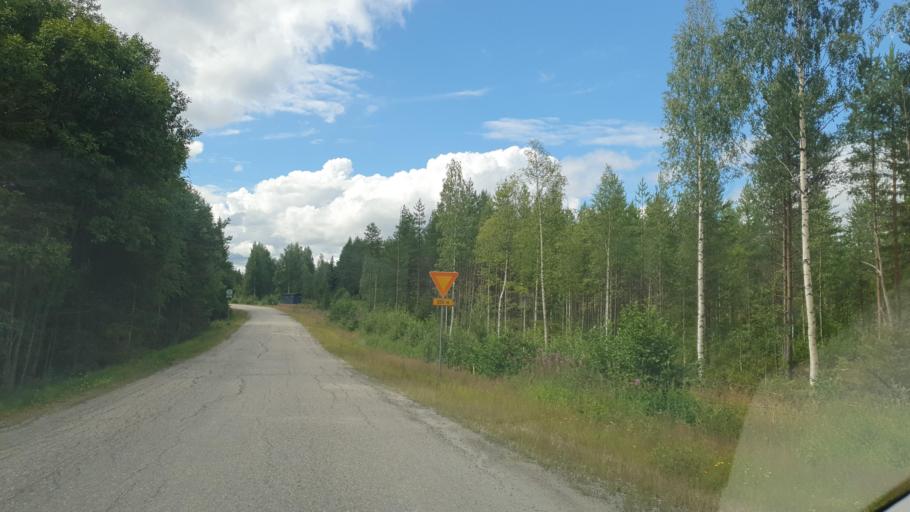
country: FI
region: Kainuu
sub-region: Kehys-Kainuu
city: Kuhmo
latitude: 64.1069
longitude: 29.3412
